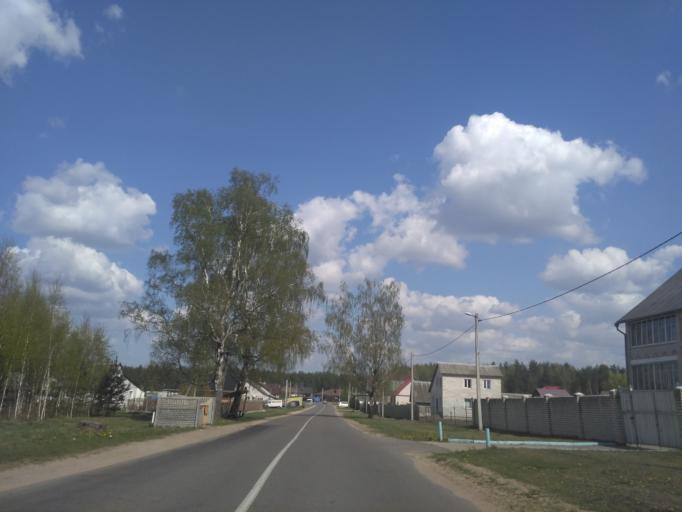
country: BY
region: Minsk
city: Radashkovichy
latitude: 54.1658
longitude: 27.2462
